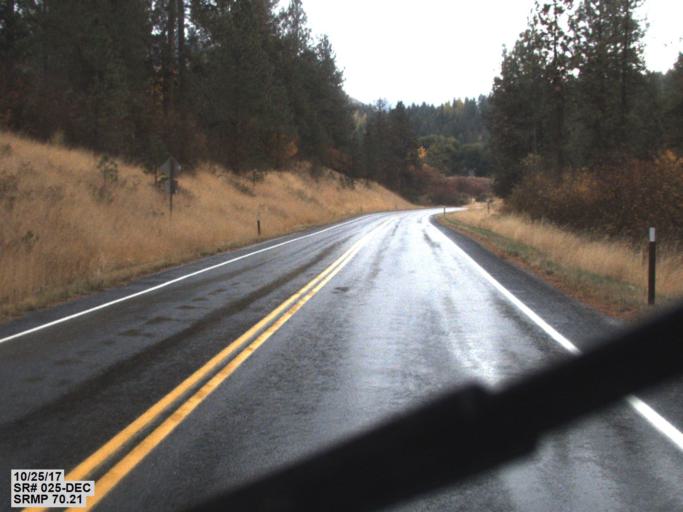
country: US
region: Washington
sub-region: Stevens County
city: Kettle Falls
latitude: 48.4798
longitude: -118.1713
